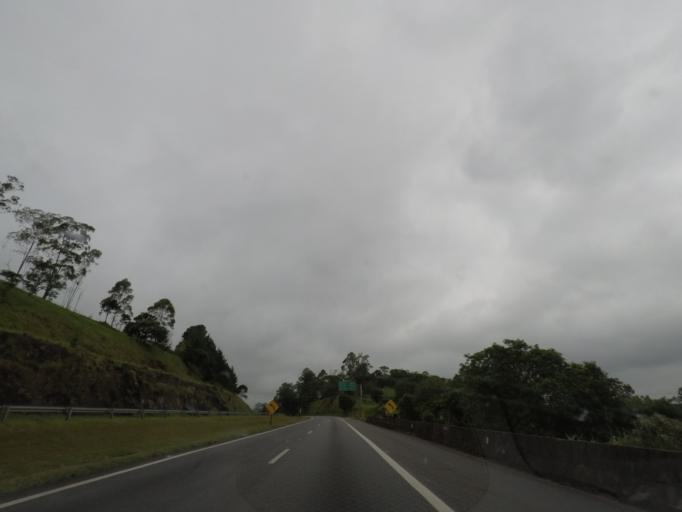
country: BR
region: Sao Paulo
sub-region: Bom Jesus Dos Perdoes
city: Bom Jesus dos Perdoes
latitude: -23.1746
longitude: -46.3842
